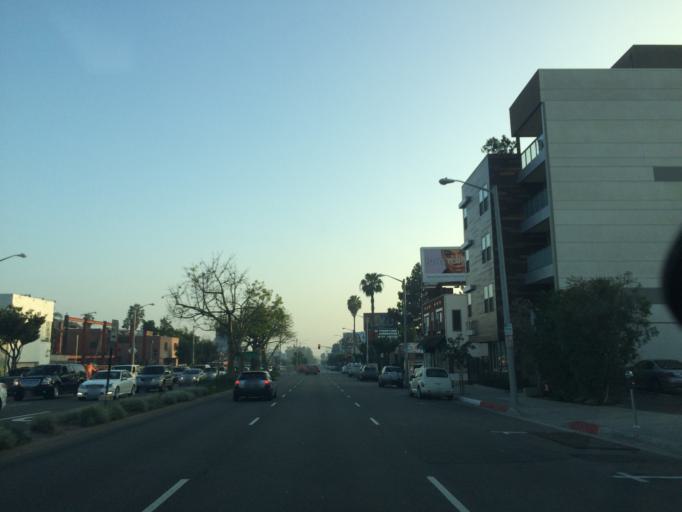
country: US
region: California
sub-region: Los Angeles County
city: West Hollywood
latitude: 34.0887
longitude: -118.3615
